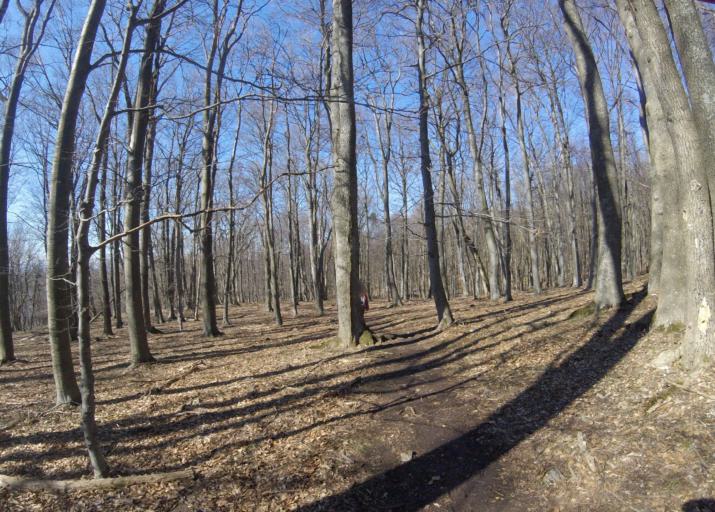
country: HU
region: Heves
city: Szilvasvarad
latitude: 48.0565
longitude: 20.4601
